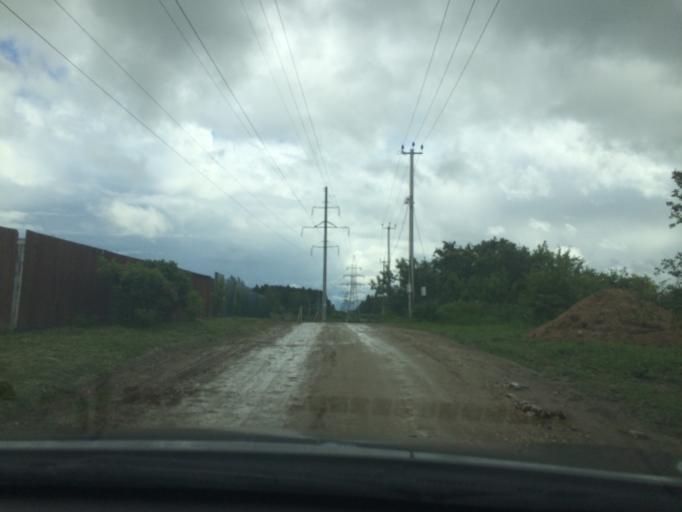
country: RU
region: Moskovskaya
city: Solnechnogorsk
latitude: 56.1634
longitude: 37.0089
